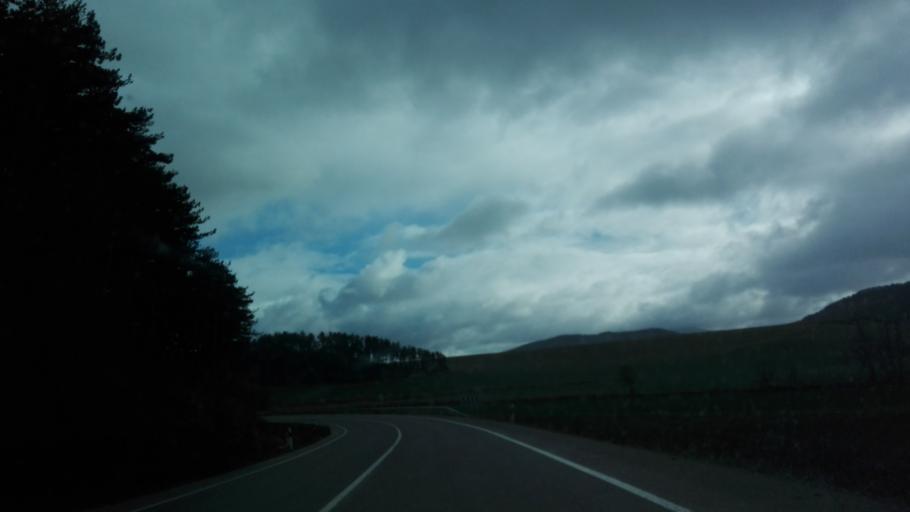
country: ES
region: Navarre
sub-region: Provincia de Navarra
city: Lizoain
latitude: 42.7989
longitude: -1.4906
